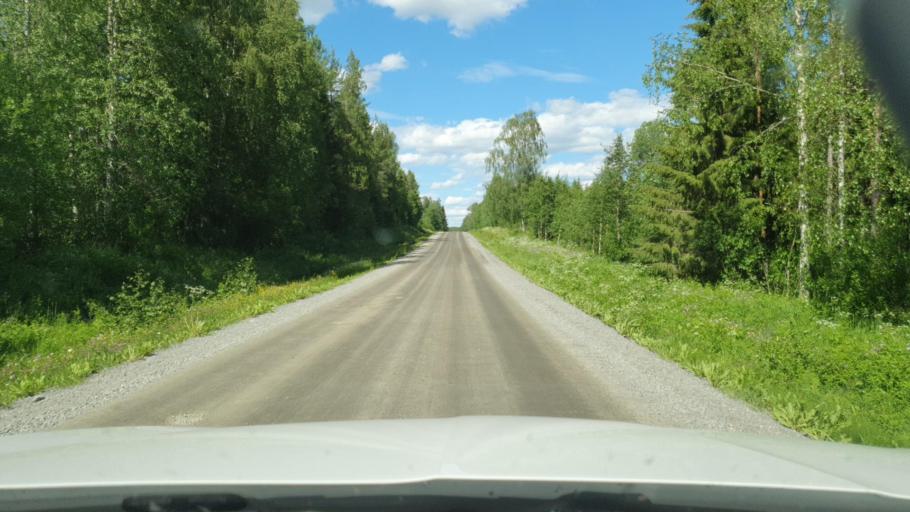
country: SE
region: Vaesterbotten
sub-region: Skelleftea Kommun
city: Forsbacka
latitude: 64.7799
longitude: 20.5147
